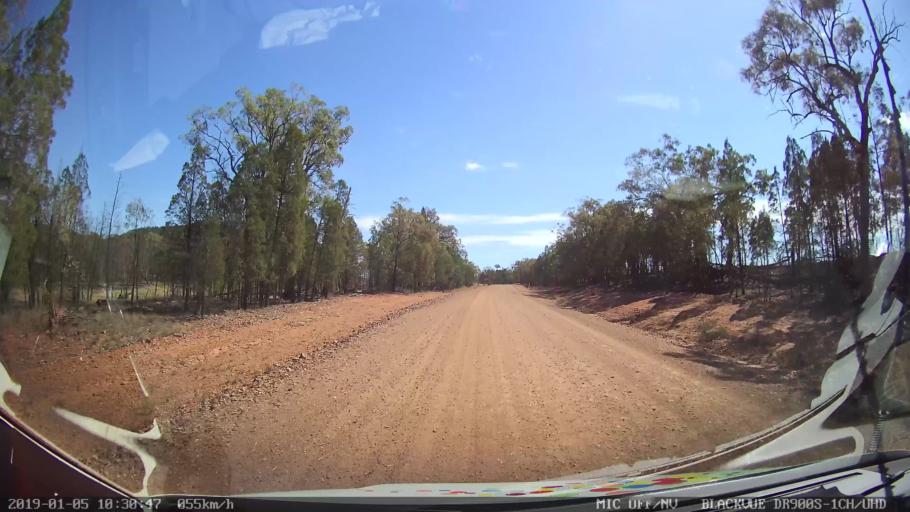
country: AU
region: New South Wales
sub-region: Gilgandra
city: Gilgandra
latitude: -31.5294
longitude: 148.9254
